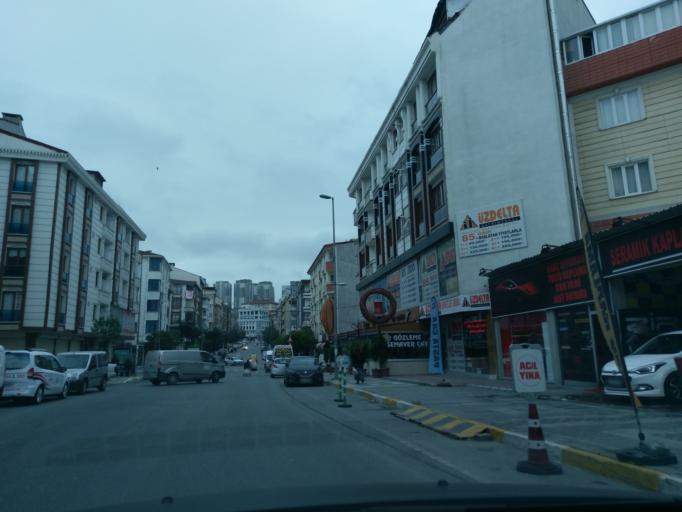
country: TR
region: Istanbul
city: Esenyurt
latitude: 41.0155
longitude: 28.6641
